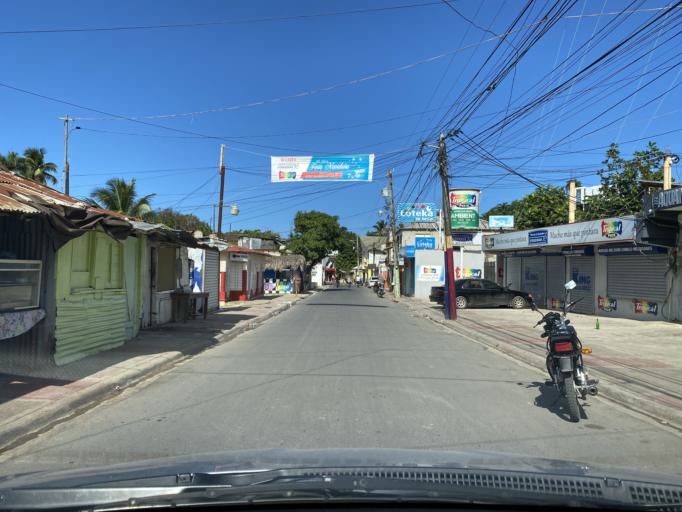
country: DO
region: Samana
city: Las Terrenas
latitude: 19.3136
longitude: -69.5416
